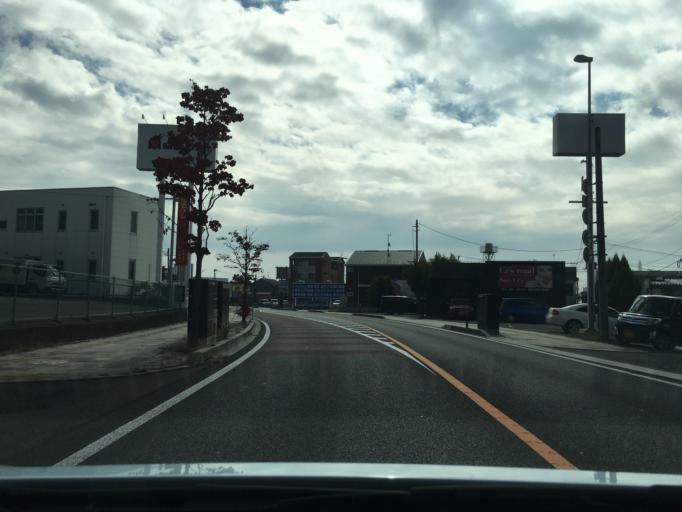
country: JP
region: Fukushima
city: Koriyama
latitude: 37.3874
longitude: 140.3555
